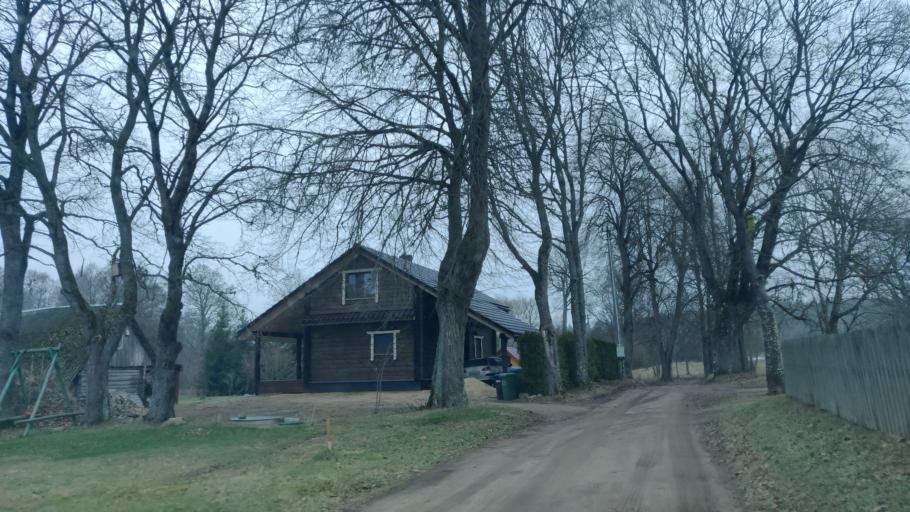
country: LT
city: Trakai
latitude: 54.5598
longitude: 24.9298
